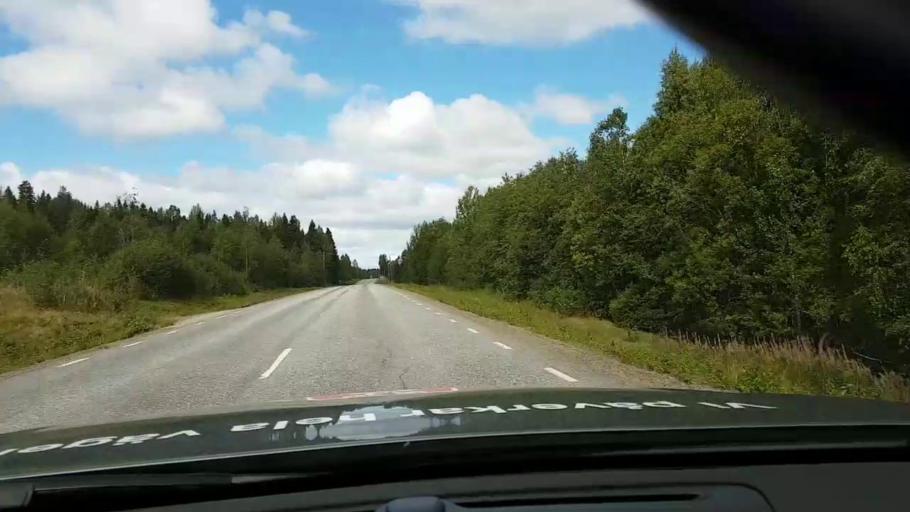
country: SE
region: Vaesternorrland
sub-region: OErnskoeldsviks Kommun
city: Bredbyn
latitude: 63.4728
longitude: 18.0977
